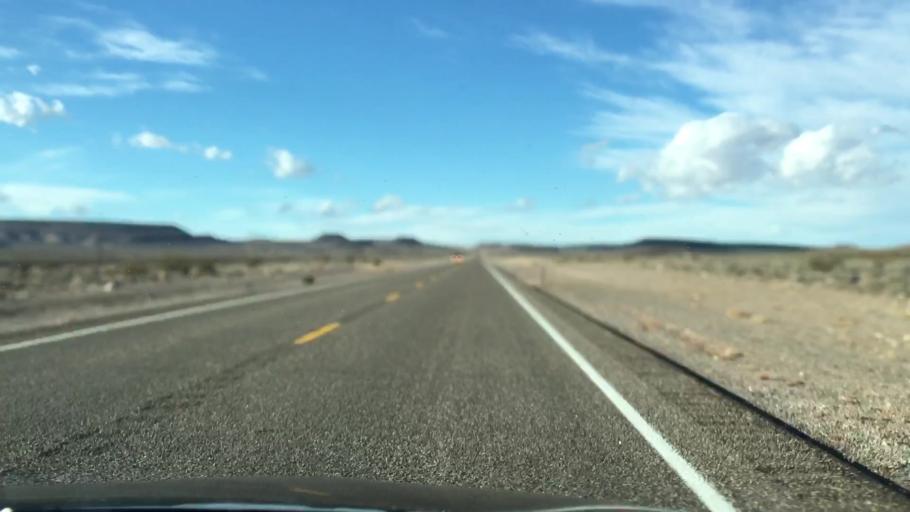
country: US
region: Nevada
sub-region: Esmeralda County
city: Goldfield
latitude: 37.3552
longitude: -117.1106
